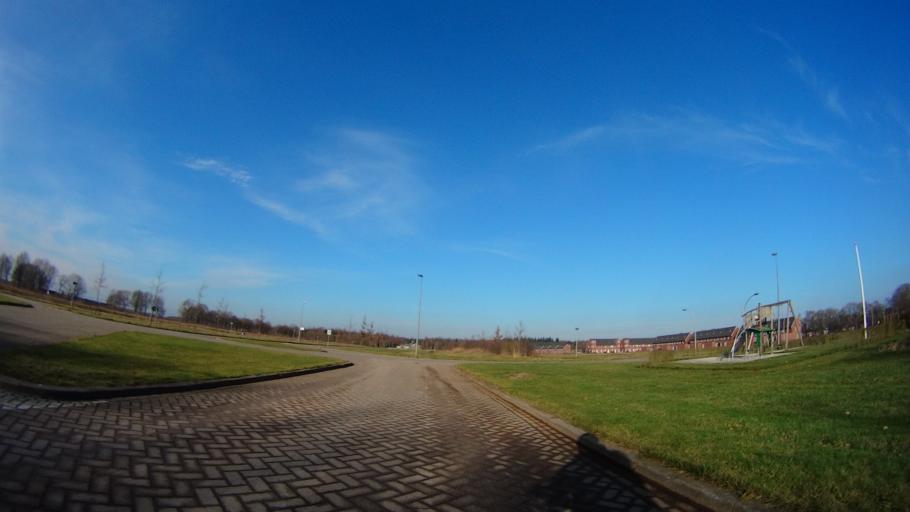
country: NL
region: Drenthe
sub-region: Gemeente Emmen
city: Emmen
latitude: 52.7543
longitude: 6.8580
